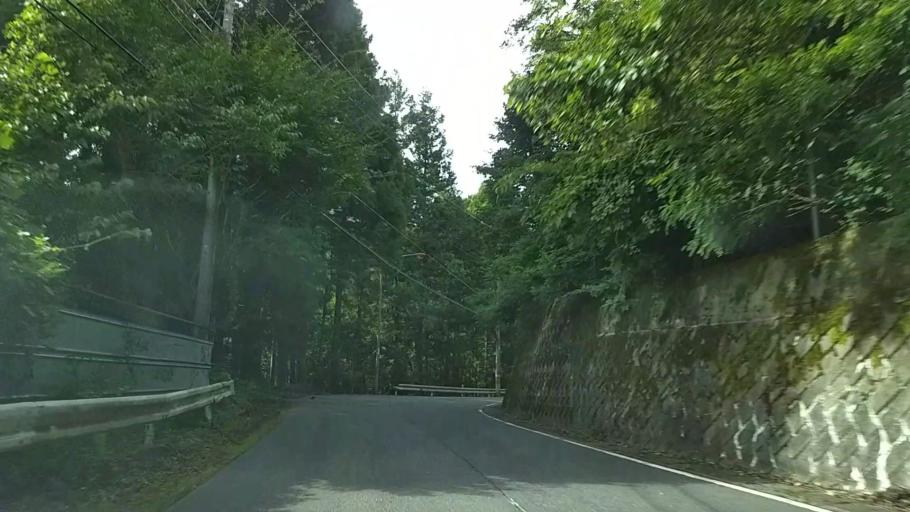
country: JP
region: Yamanashi
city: Uenohara
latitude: 35.5793
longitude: 139.1507
